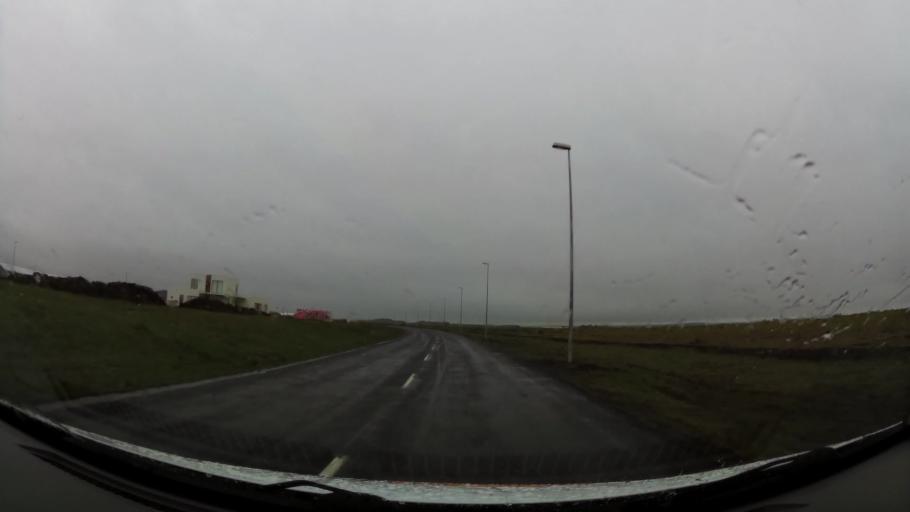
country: IS
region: South
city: Selfoss
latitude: 63.9234
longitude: -20.9865
